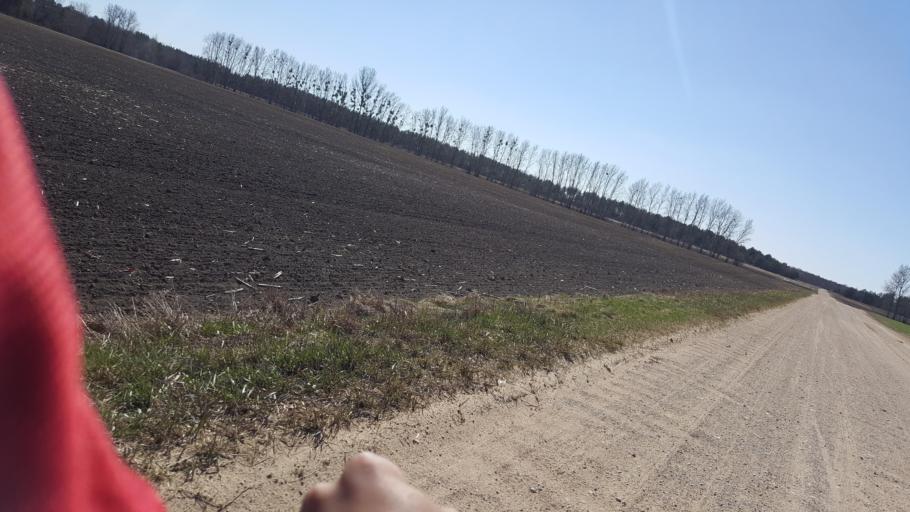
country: BY
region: Brest
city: Kamyanyets
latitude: 52.3137
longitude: 23.8624
